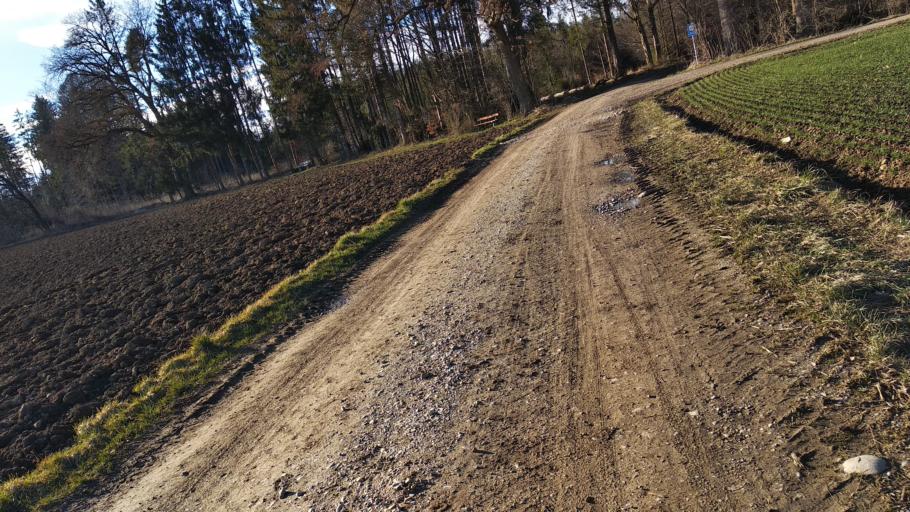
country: DE
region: Bavaria
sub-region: Upper Bavaria
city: Aying
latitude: 47.9834
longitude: 11.7665
